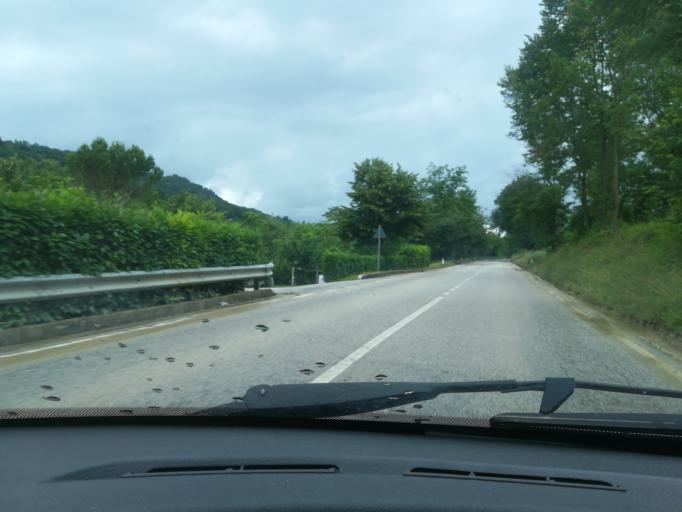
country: IT
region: The Marches
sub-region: Provincia di Macerata
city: San Ginesio
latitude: 43.0990
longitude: 13.3425
